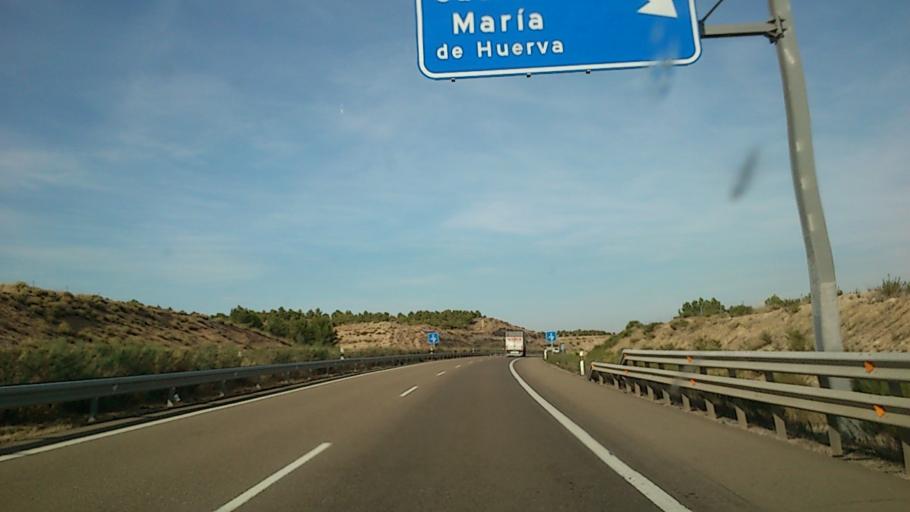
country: ES
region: Aragon
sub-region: Provincia de Zaragoza
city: Maria de Huerva
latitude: 41.5514
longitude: -0.9921
